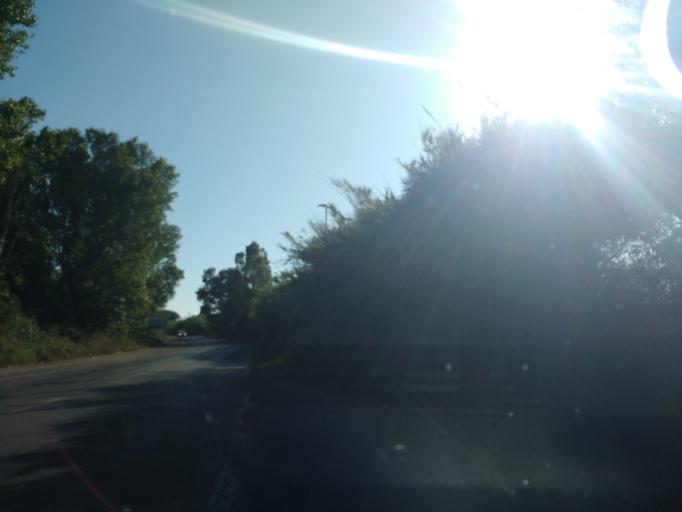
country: IT
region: Latium
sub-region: Citta metropolitana di Roma Capitale
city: Maccarese
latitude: 41.8757
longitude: 12.2125
